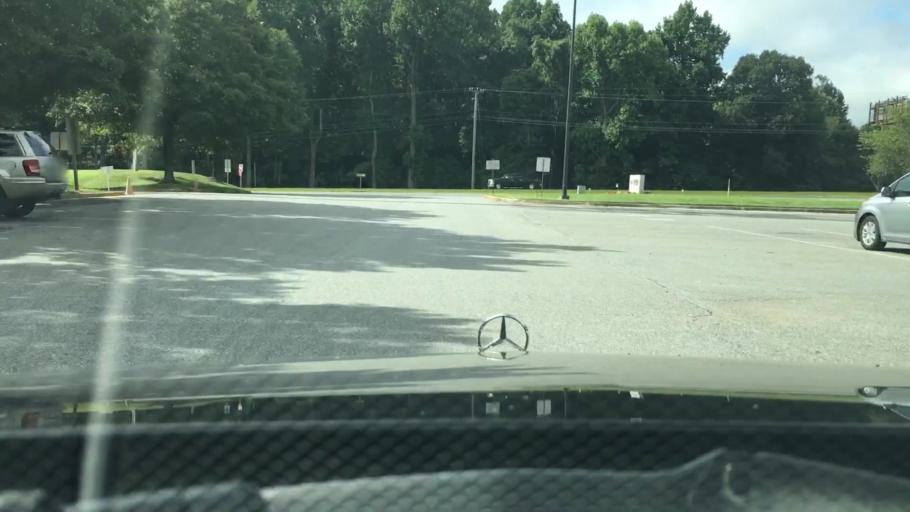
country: US
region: Virginia
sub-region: Campbell County
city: Timberlake
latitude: 37.3060
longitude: -79.2967
